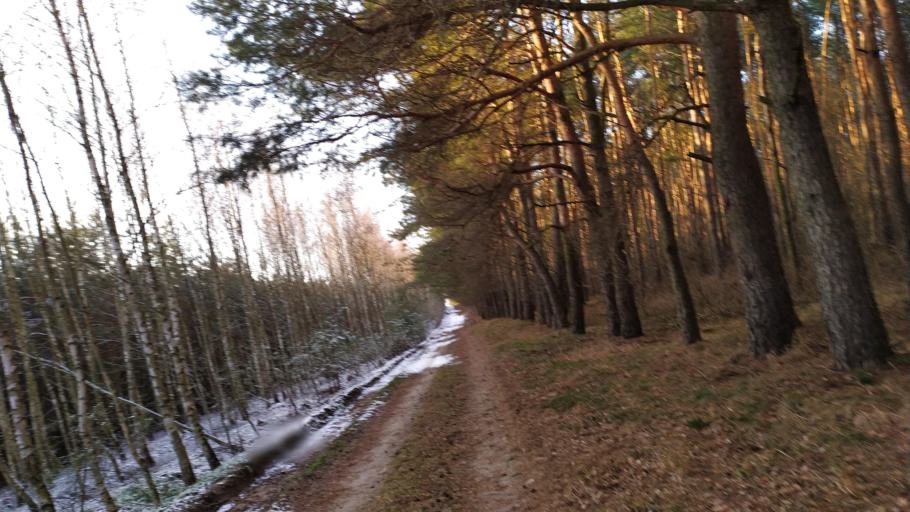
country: BY
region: Brest
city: Kamyanyets
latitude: 52.3851
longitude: 23.8287
